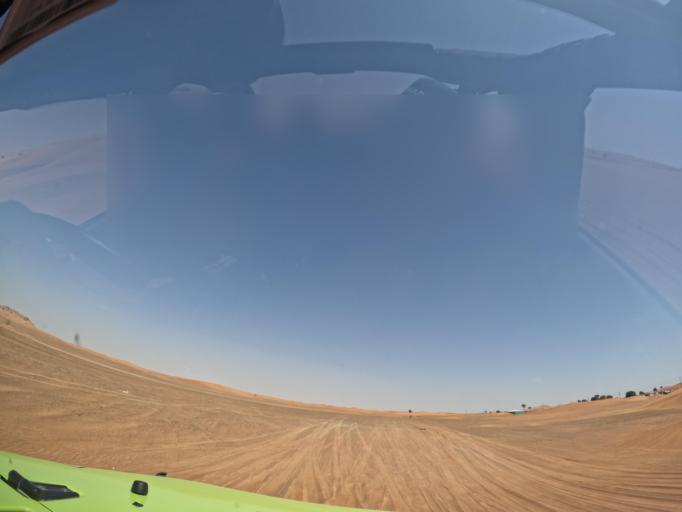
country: AE
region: Ash Shariqah
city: Adh Dhayd
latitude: 25.0125
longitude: 55.7421
